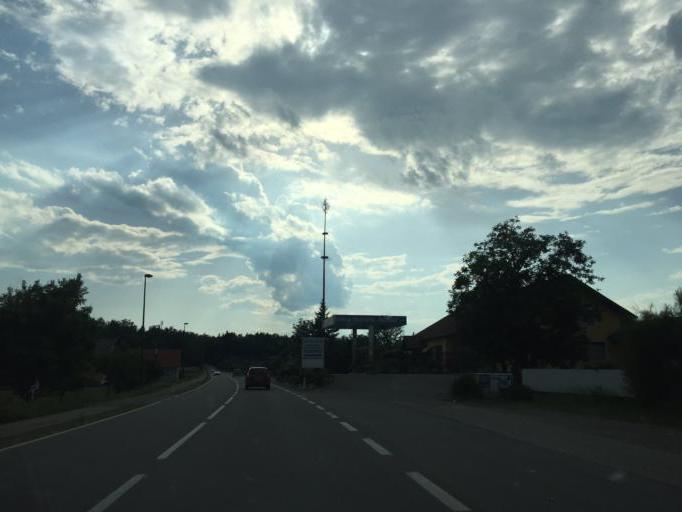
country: AT
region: Styria
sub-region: Politischer Bezirk Leibnitz
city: Strass in Steiermark
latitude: 46.7591
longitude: 15.6635
